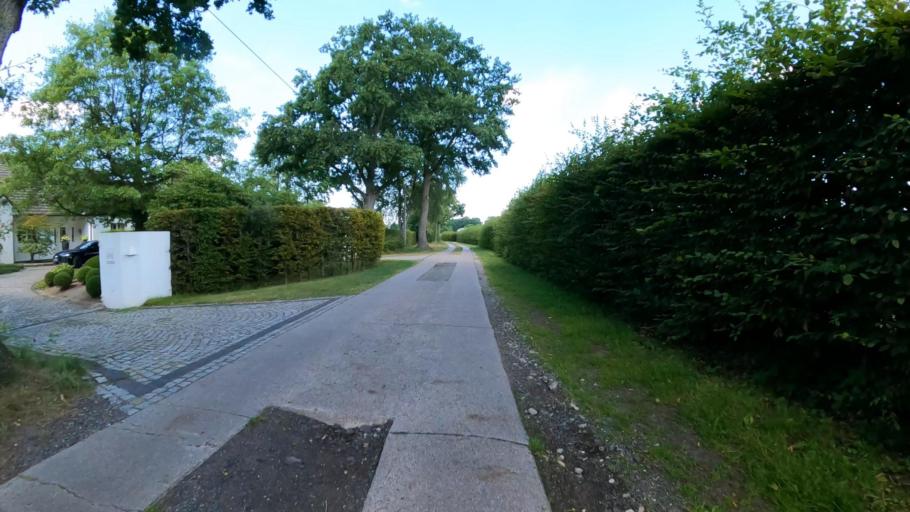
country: DE
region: Schleswig-Holstein
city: Borstel-Hohenraden
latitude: 53.6677
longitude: 9.8266
